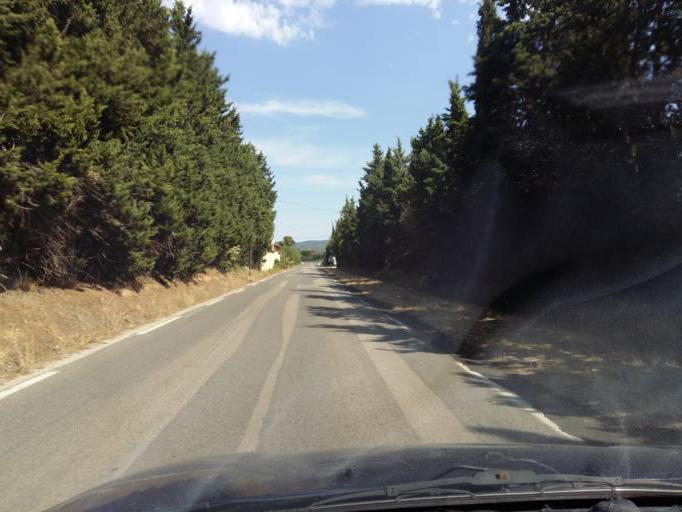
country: FR
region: Provence-Alpes-Cote d'Azur
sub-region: Departement du Vaucluse
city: Pernes-les-Fontaines
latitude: 44.0124
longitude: 5.0447
